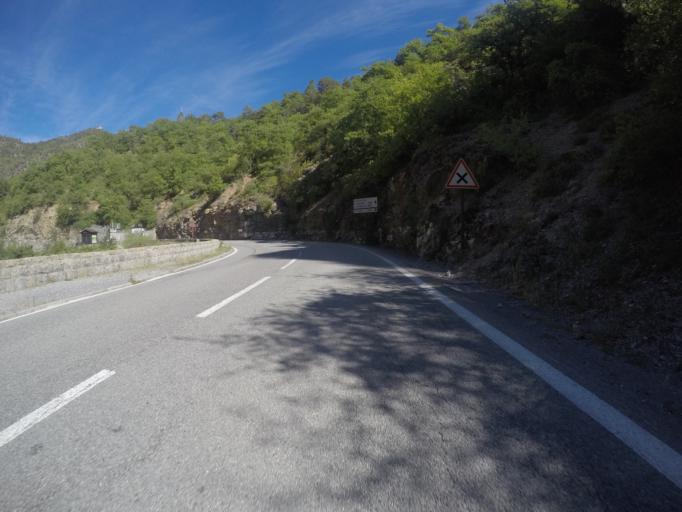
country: FR
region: Provence-Alpes-Cote d'Azur
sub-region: Departement des Alpes-Maritimes
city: Gilette
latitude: 43.9389
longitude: 7.1661
